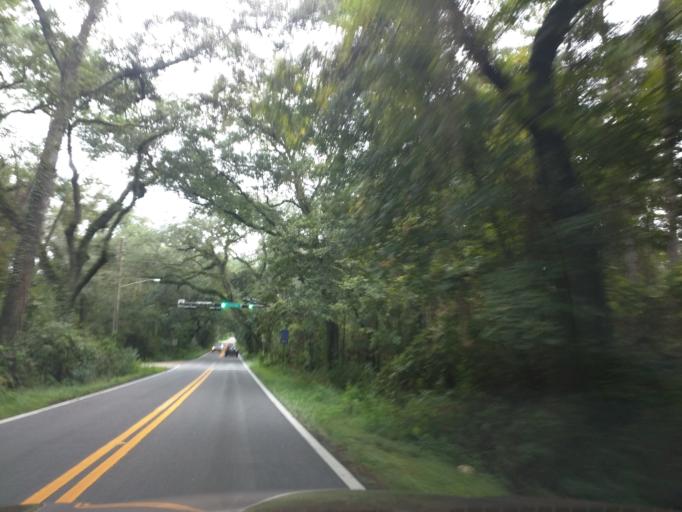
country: US
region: Florida
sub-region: Leon County
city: Tallahassee
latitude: 30.4799
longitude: -84.2098
